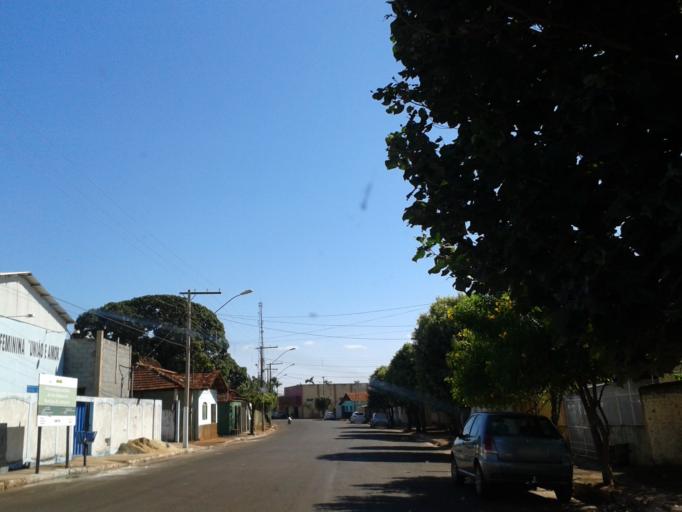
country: BR
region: Minas Gerais
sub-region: Centralina
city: Centralina
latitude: -18.5878
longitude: -49.1950
